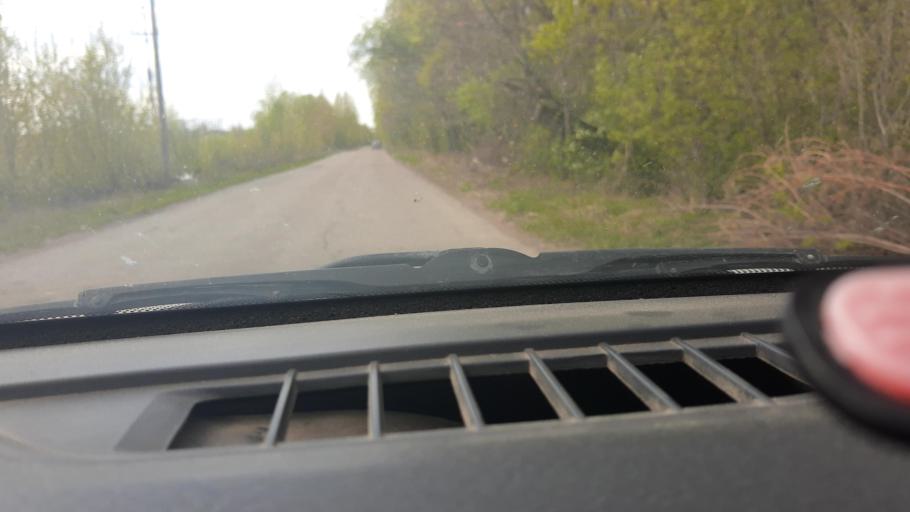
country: RU
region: Bashkortostan
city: Avdon
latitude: 54.6561
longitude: 55.8252
